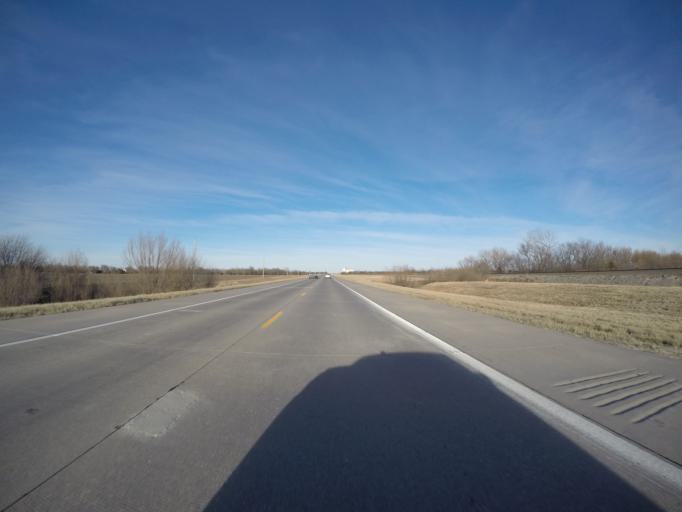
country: US
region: Kansas
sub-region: Harvey County
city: North Newton
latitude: 38.1032
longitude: -97.2730
